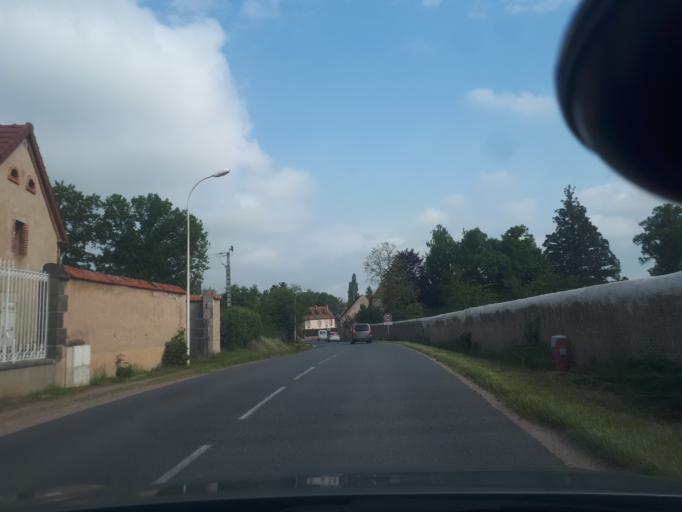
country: FR
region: Auvergne
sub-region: Departement de l'Allier
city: Lapalisse
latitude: 46.3233
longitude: 3.5859
